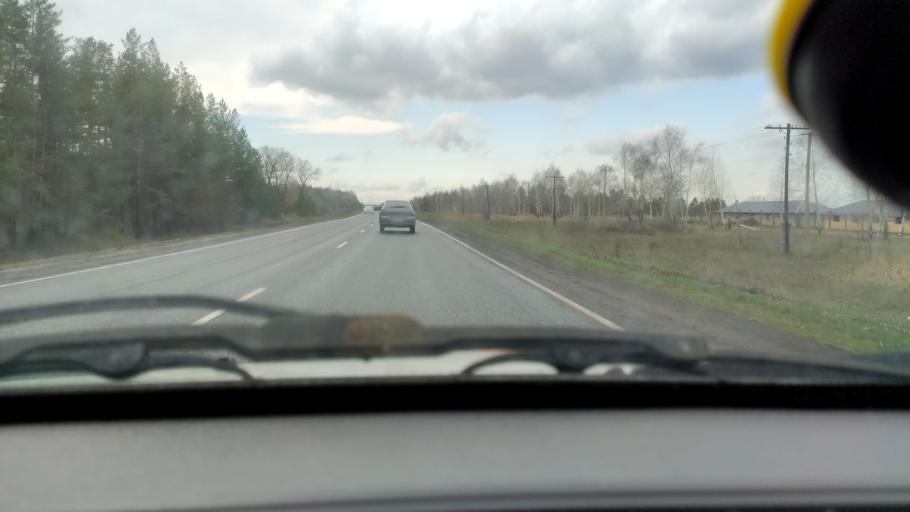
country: RU
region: Samara
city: Povolzhskiy
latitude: 53.6004
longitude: 49.5942
